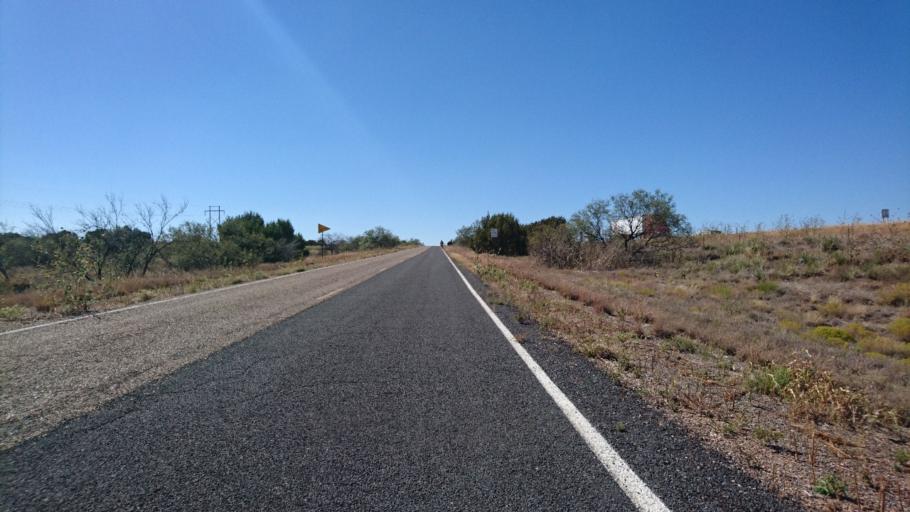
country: US
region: New Mexico
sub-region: Quay County
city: Tucumcari
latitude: 35.0700
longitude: -104.1628
